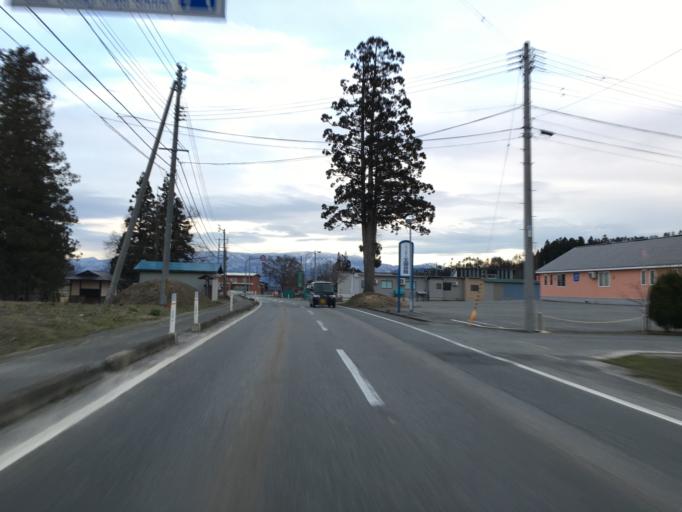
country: JP
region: Yamagata
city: Yonezawa
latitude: 37.9645
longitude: 140.0669
